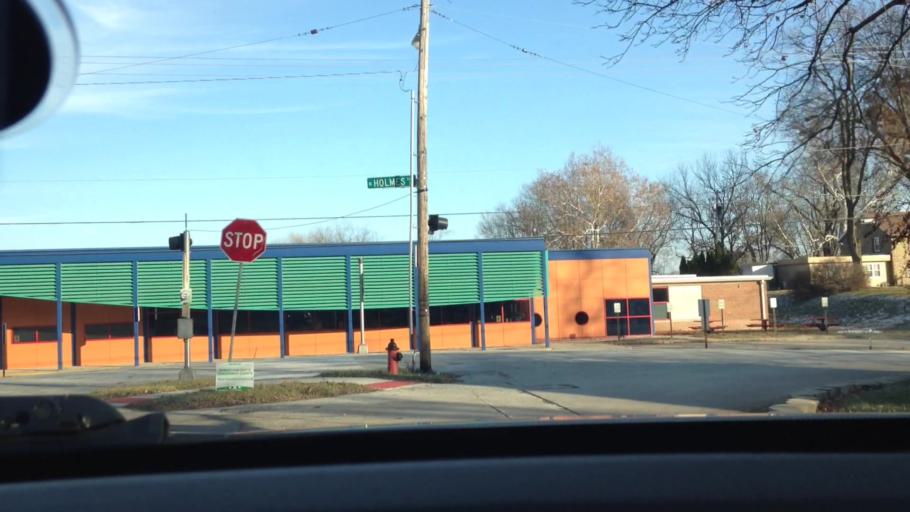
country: US
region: Missouri
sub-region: Clay County
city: Gladstone
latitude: 39.1735
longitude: -94.5725
